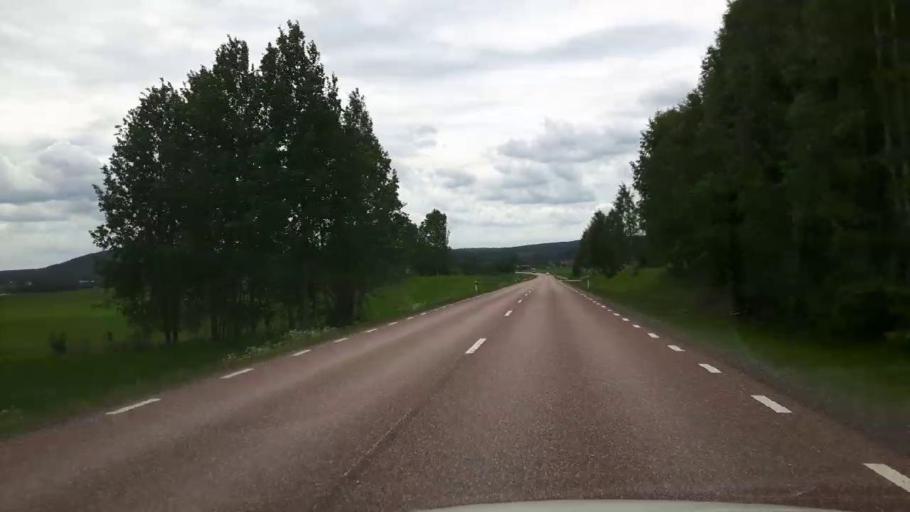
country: SE
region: Dalarna
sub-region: Hedemora Kommun
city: Brunna
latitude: 60.2426
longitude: 16.0070
